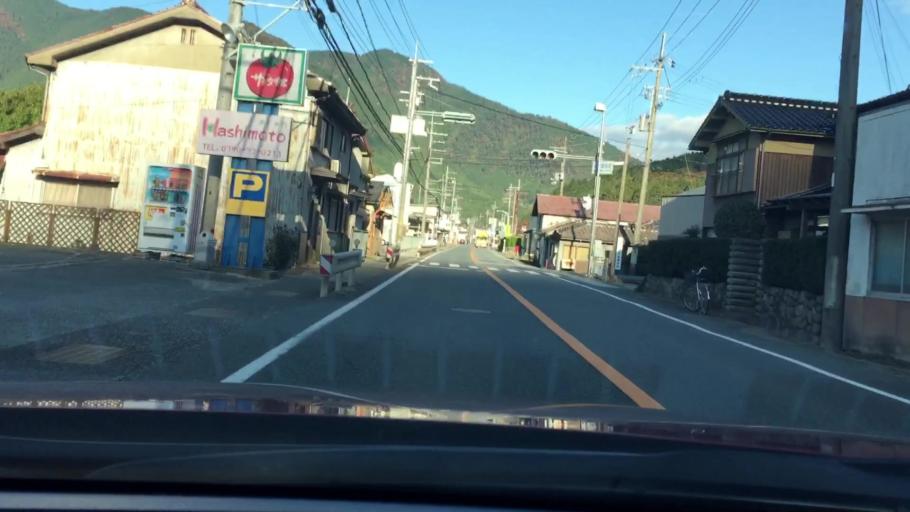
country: JP
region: Hyogo
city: Yamazakicho-nakabirose
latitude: 35.1087
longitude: 134.5791
